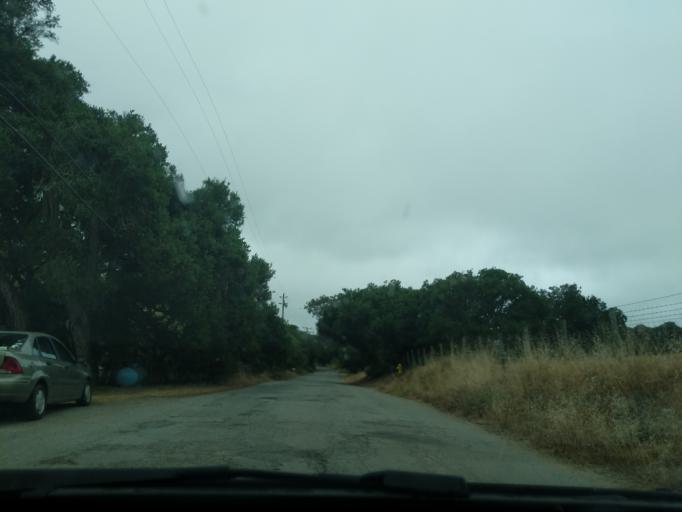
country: US
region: California
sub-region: San Benito County
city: Aromas
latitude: 36.8682
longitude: -121.6210
